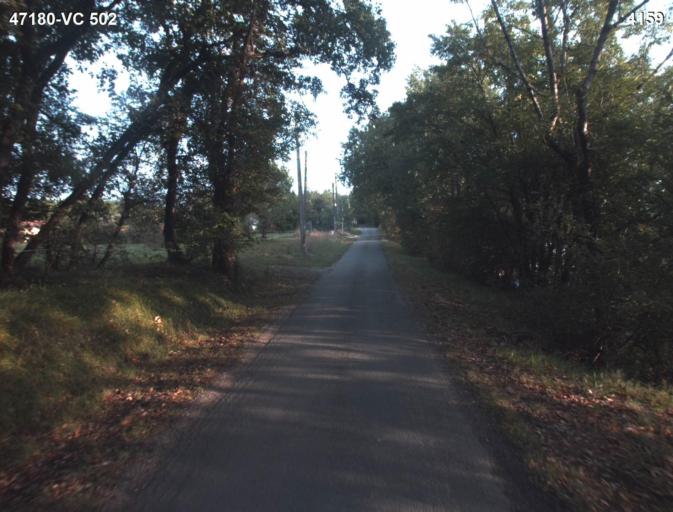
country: FR
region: Aquitaine
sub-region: Departement du Lot-et-Garonne
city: Sainte-Colombe-en-Bruilhois
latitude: 44.1938
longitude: 0.4809
